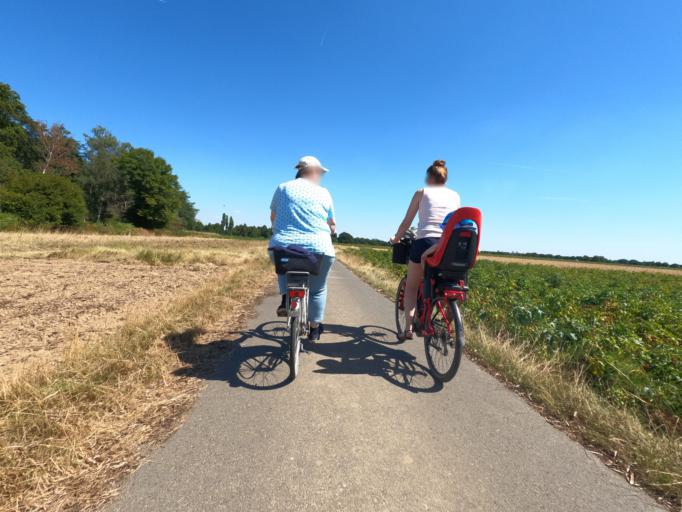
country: DE
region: North Rhine-Westphalia
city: Wegberg
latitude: 51.1199
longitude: 6.2838
